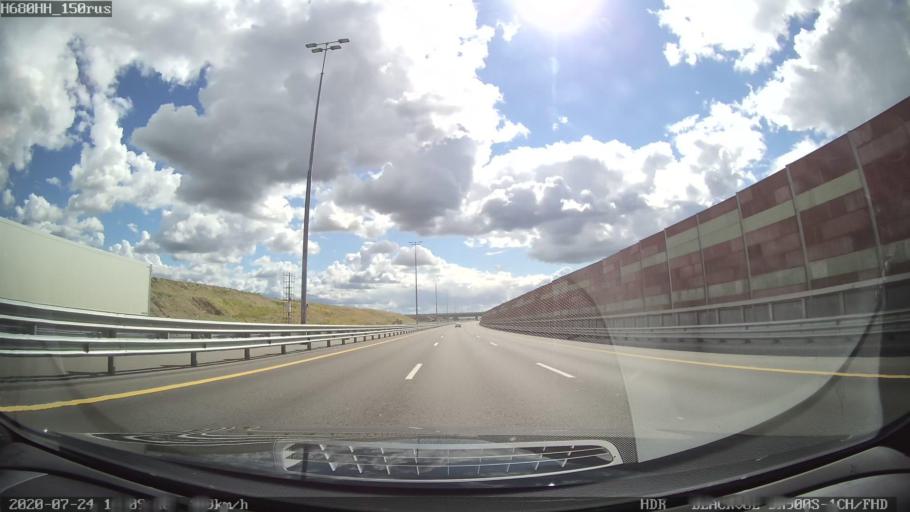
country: RU
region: St.-Petersburg
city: Tyarlevo
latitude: 59.7473
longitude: 30.4825
